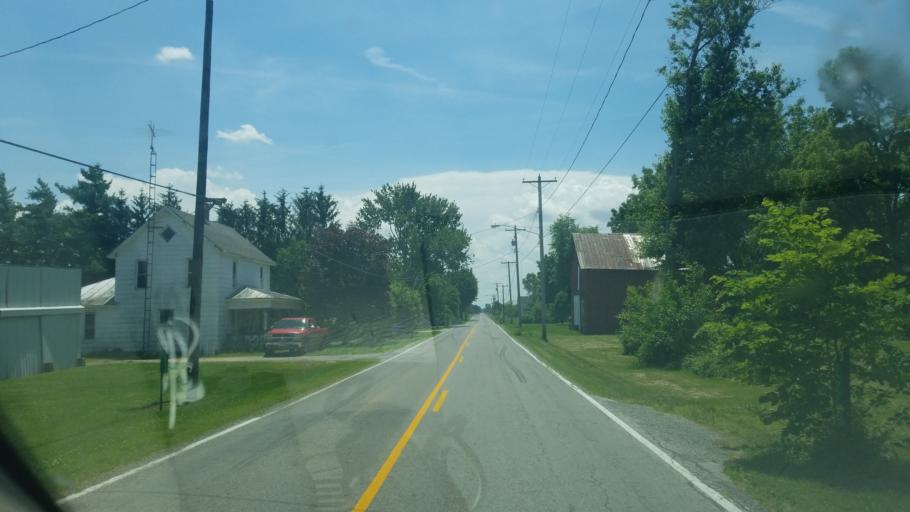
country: US
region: Ohio
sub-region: Hancock County
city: Arlington
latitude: 40.9345
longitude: -83.5945
